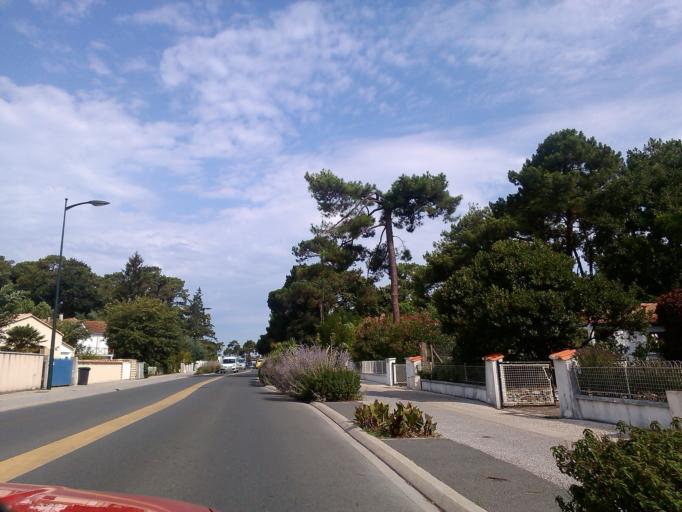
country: FR
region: Poitou-Charentes
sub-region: Departement de la Charente-Maritime
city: La Tremblade
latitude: 45.7908
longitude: -1.1599
